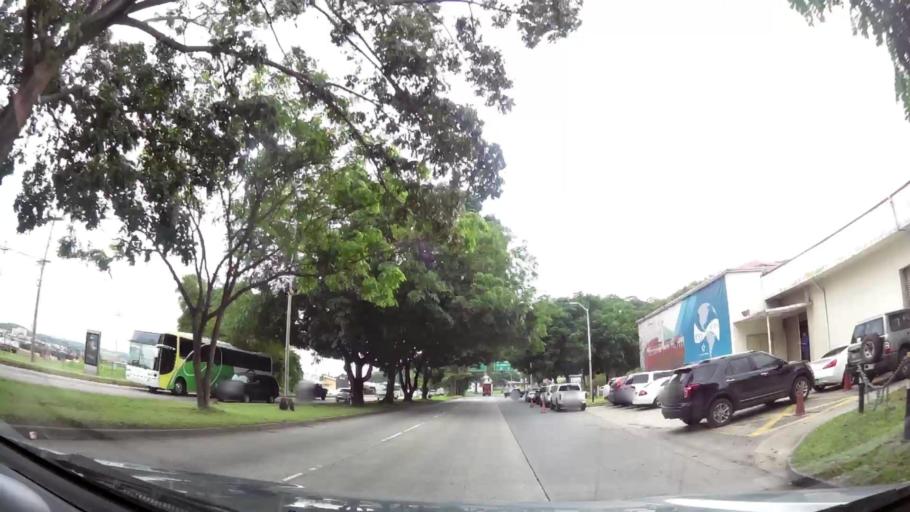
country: PA
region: Panama
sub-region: Distrito de Panama
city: Ancon
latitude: 8.9598
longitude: -79.5568
